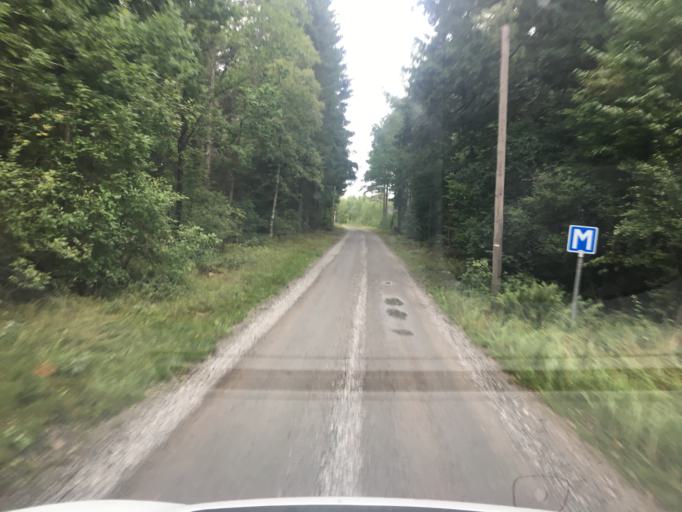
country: SE
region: Kronoberg
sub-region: Ljungby Kommun
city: Lagan
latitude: 56.9686
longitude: 14.0412
